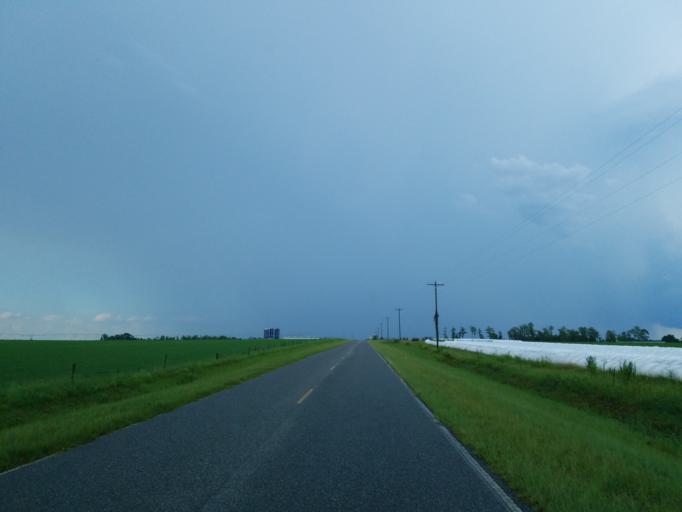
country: US
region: Georgia
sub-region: Cook County
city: Adel
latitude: 31.0762
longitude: -83.4343
